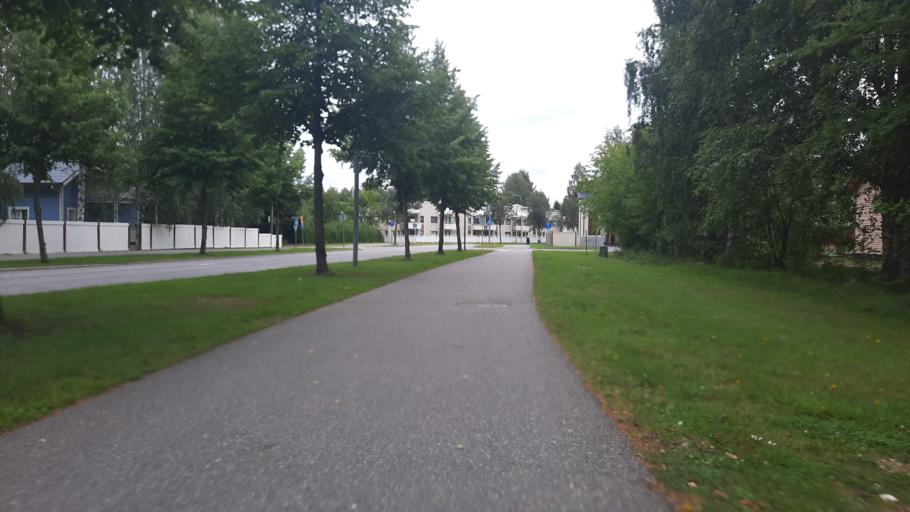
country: FI
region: North Karelia
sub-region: Joensuu
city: Joensuu
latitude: 62.6215
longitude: 29.8581
